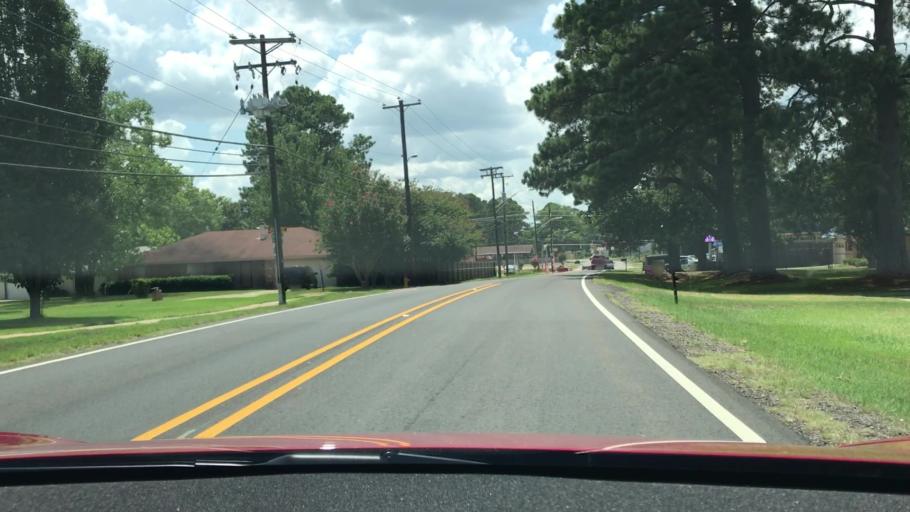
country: US
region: Louisiana
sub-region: De Soto Parish
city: Stonewall
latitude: 32.3910
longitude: -93.7784
